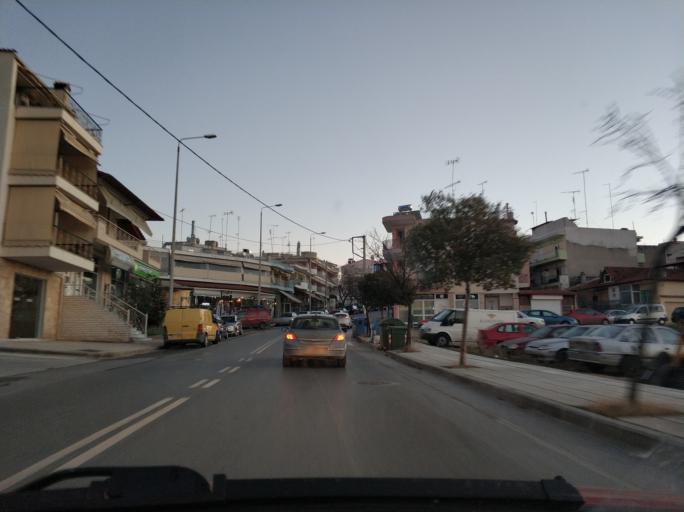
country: GR
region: Central Macedonia
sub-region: Nomos Thessalonikis
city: Polichni
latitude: 40.6661
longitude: 22.9467
